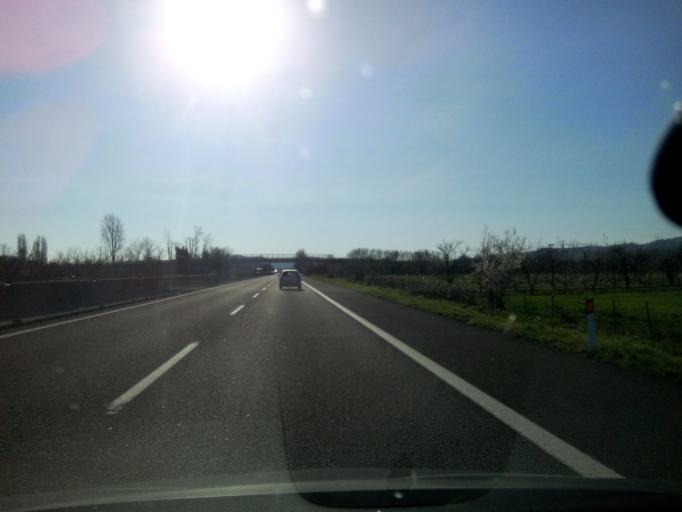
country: IT
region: Emilia-Romagna
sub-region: Provincia di Bologna
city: Zola Predosa
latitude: 44.5014
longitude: 11.2173
